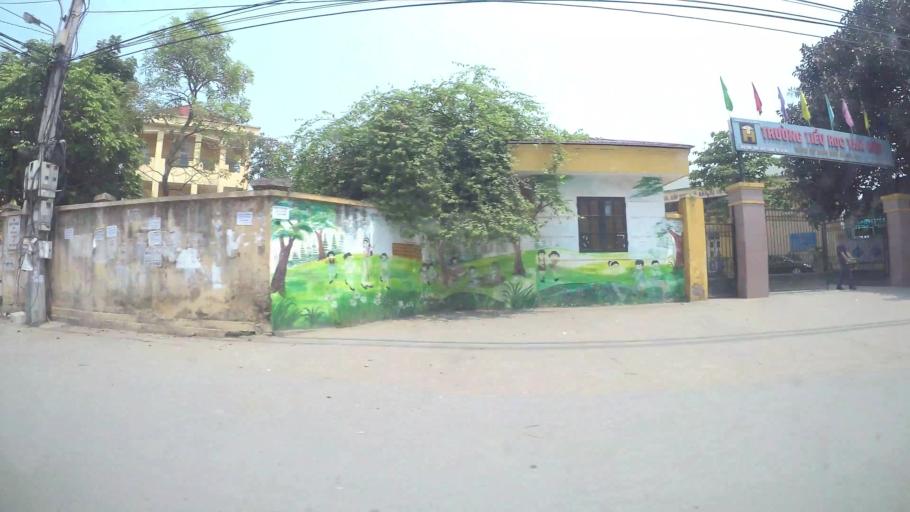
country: VN
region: Ha Noi
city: Van Dien
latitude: 20.9503
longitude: 105.8307
